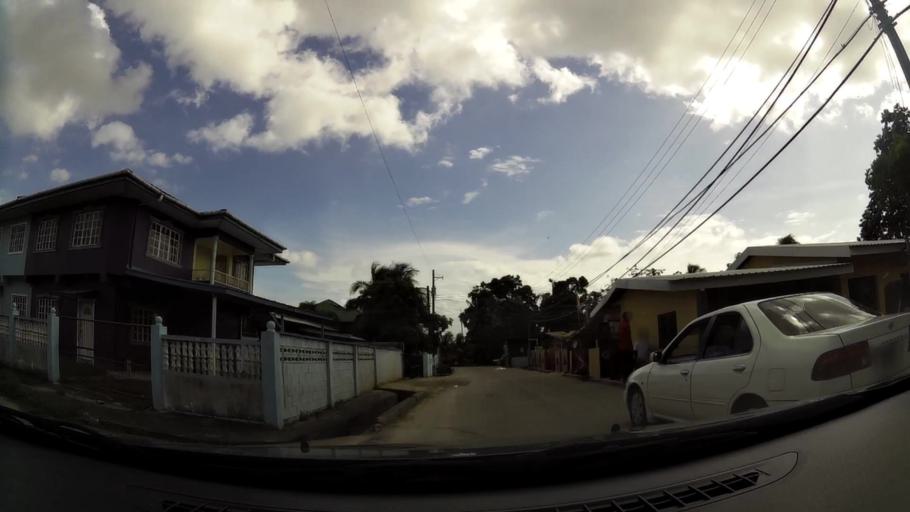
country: TT
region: Tunapuna/Piarco
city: Arouca
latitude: 10.6165
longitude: -61.3256
